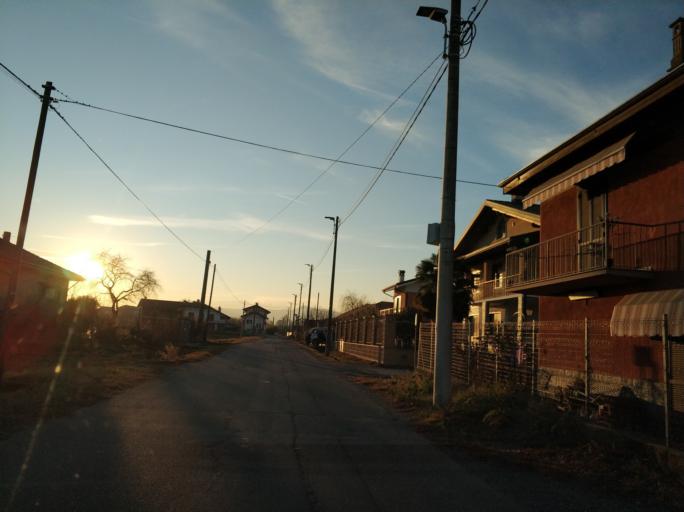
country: IT
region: Piedmont
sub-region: Provincia di Torino
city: Caselle Torinese
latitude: 45.1816
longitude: 7.6386
